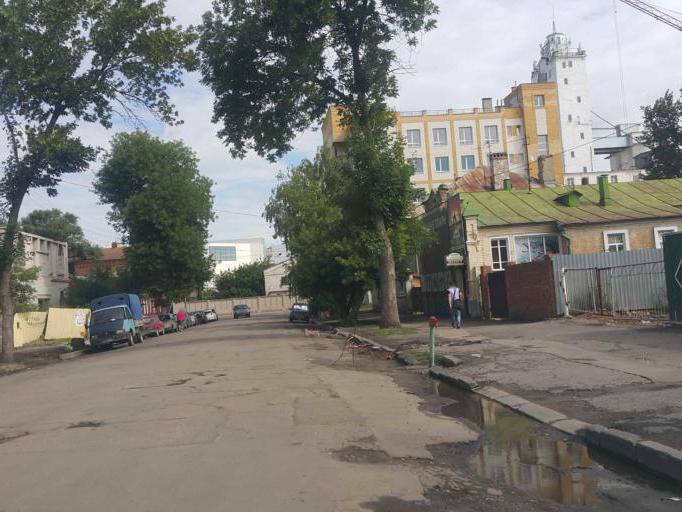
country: RU
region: Tambov
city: Tambov
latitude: 52.7260
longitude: 41.4465
